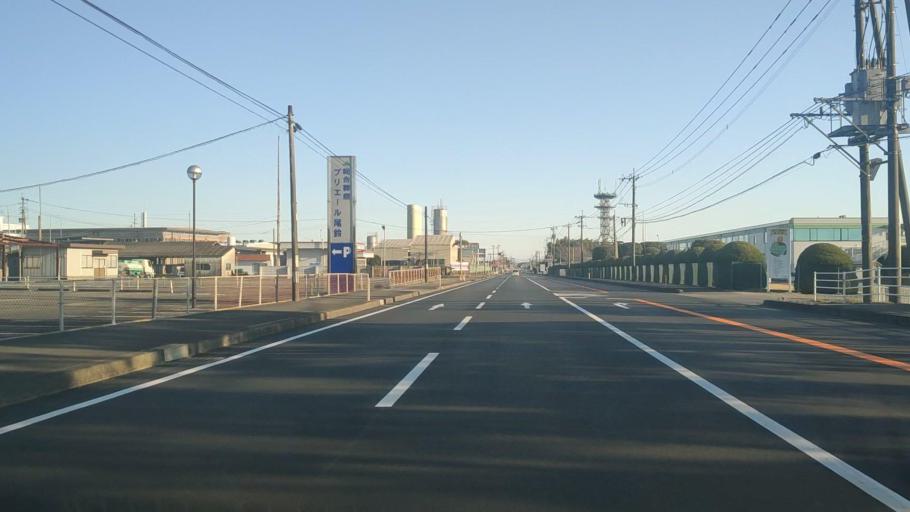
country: JP
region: Miyazaki
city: Takanabe
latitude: 32.2224
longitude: 131.5426
